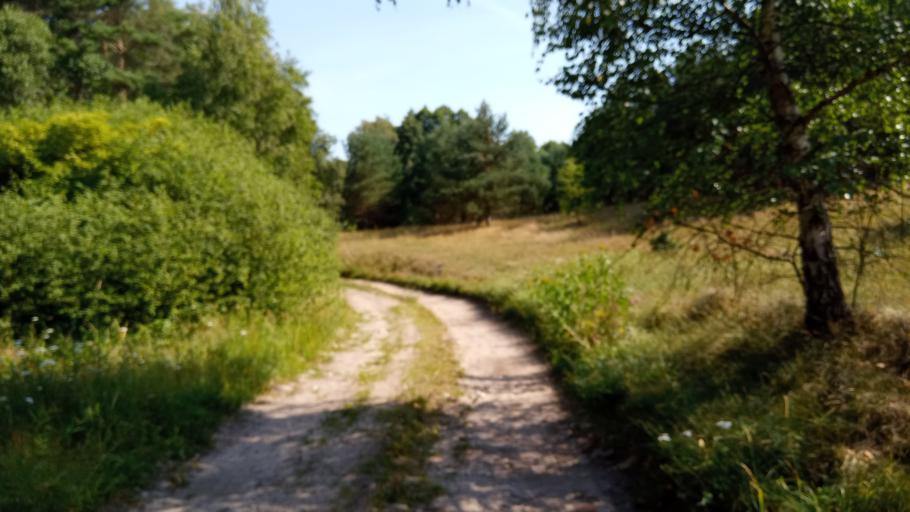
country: PL
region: West Pomeranian Voivodeship
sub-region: Powiat szczecinecki
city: Lubowo
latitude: 53.6328
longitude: 16.3482
